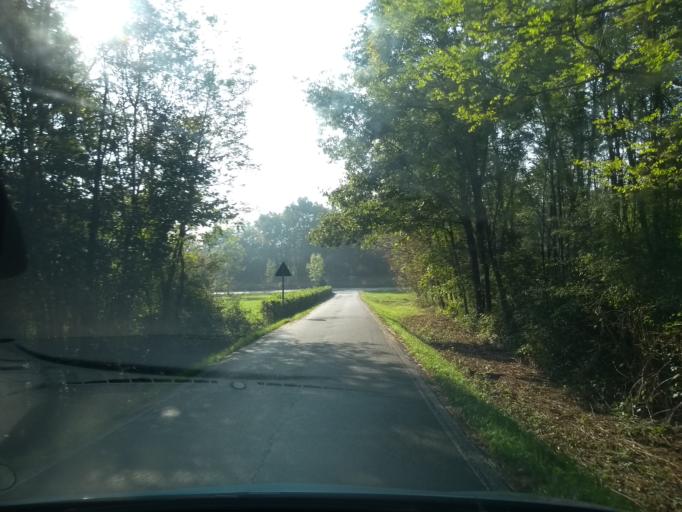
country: IT
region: Piedmont
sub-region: Provincia di Torino
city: Fiano
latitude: 45.2176
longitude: 7.5108
